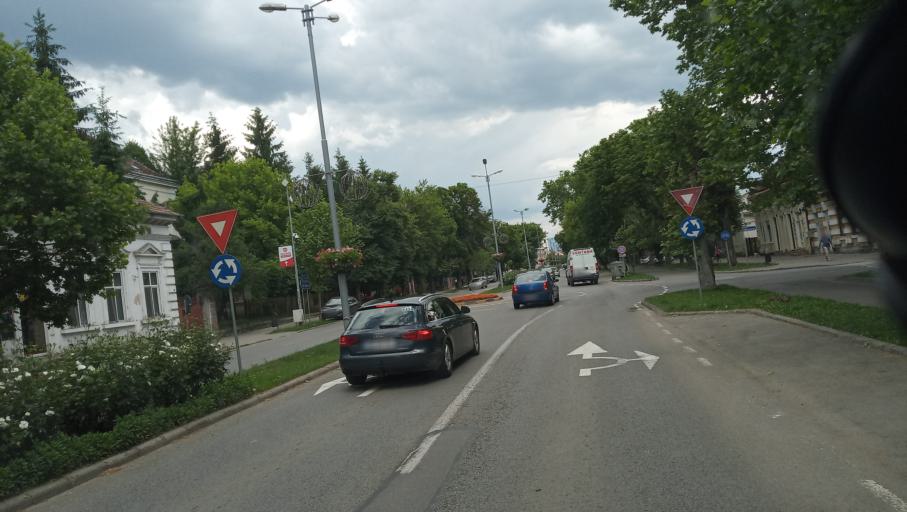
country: RO
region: Bistrita-Nasaud
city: Bistrita
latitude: 47.1281
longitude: 24.4873
